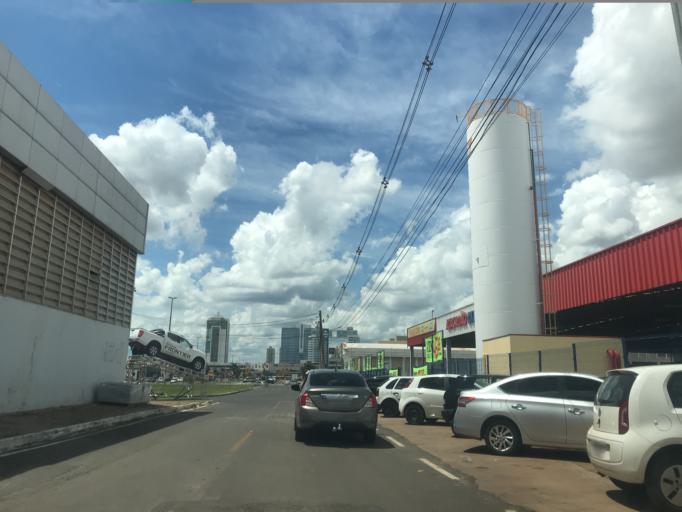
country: BR
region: Federal District
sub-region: Brasilia
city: Brasilia
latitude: -15.8492
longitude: -48.0406
